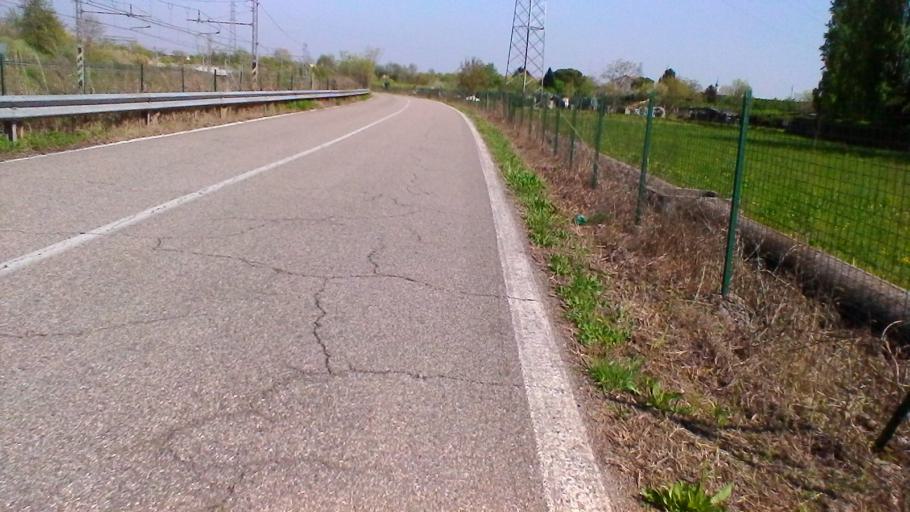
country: IT
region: Veneto
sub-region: Provincia di Verona
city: Verona
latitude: 45.4263
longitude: 10.9425
